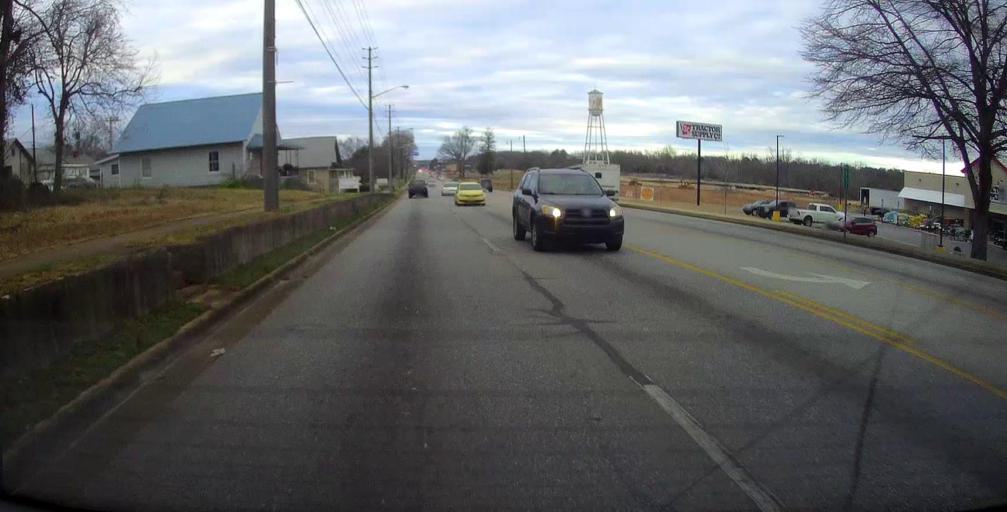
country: US
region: Alabama
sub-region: Chambers County
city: Lanett
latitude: 32.8610
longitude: -85.1901
